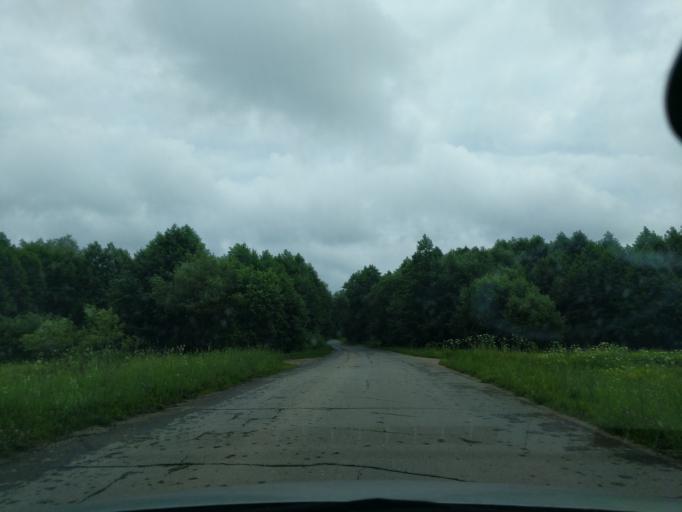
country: RU
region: Kaluga
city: Myatlevo
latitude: 54.8356
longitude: 35.6373
